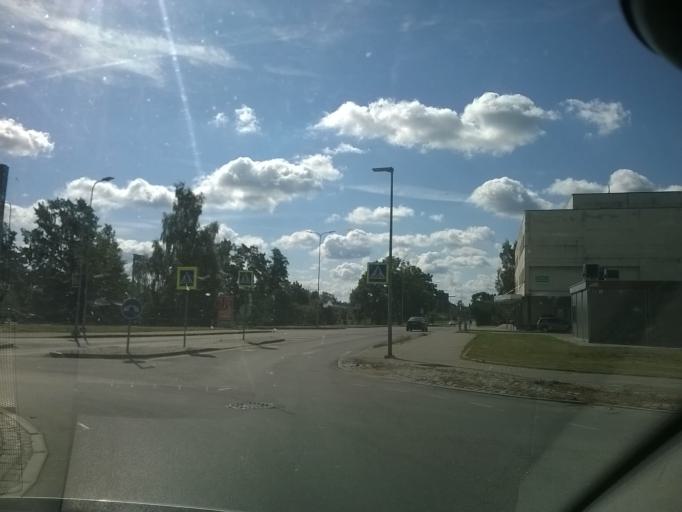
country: EE
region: Vorumaa
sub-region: Voru linn
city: Voru
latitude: 57.8424
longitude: 27.0058
